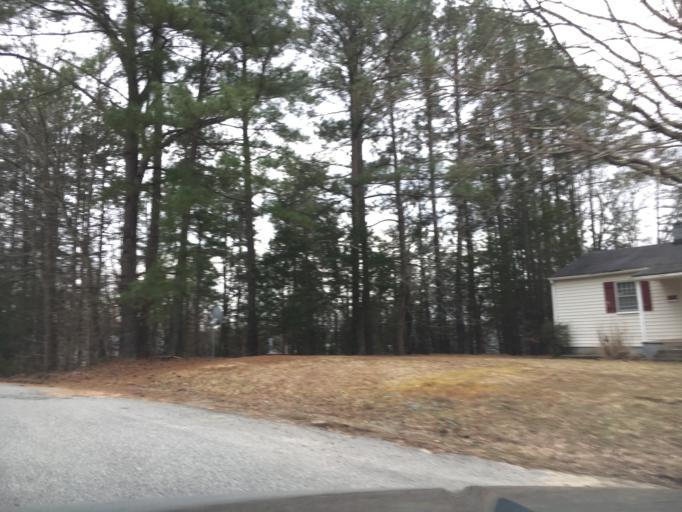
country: US
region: Virginia
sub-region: Halifax County
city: South Boston
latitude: 36.7014
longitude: -78.9128
